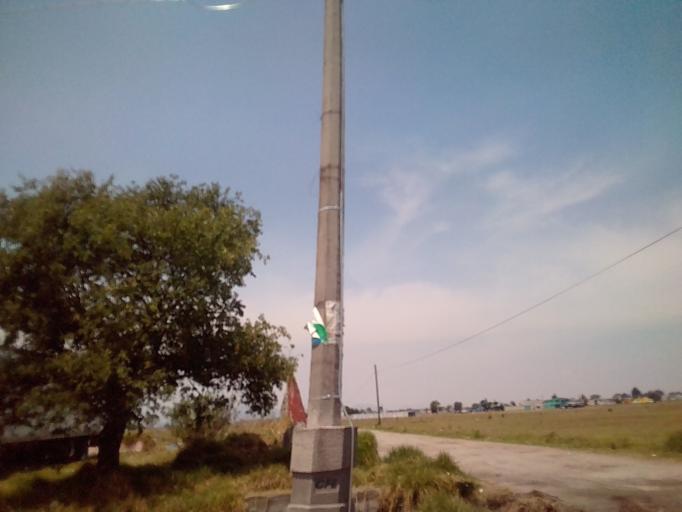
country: MX
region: Mexico
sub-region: Toluca
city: Guadalupe Totoltepec
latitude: 19.3561
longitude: -99.5600
